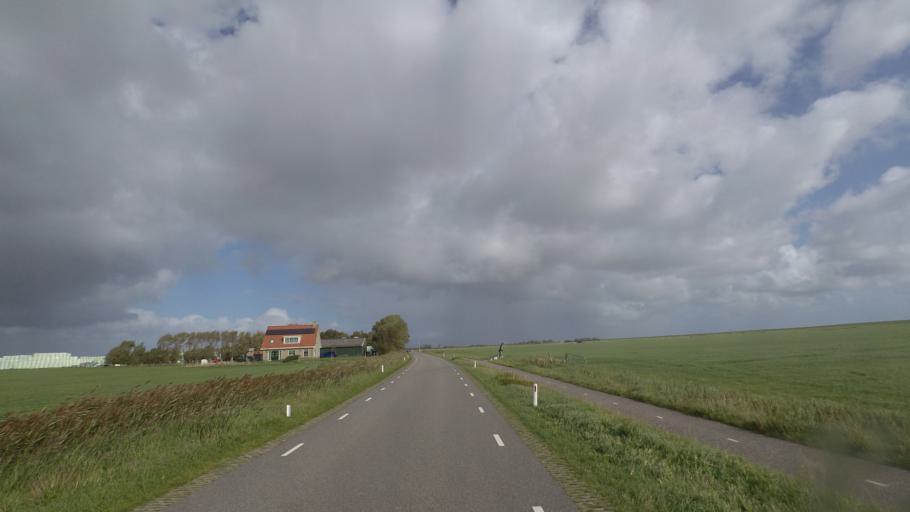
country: NL
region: Friesland
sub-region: Gemeente Ameland
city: Hollum
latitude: 53.4371
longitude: 5.6686
